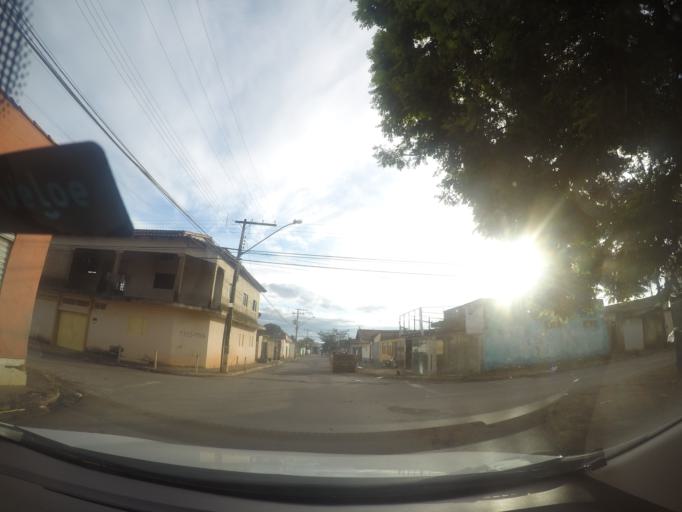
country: BR
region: Goias
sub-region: Goiania
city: Goiania
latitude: -16.6462
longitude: -49.3272
